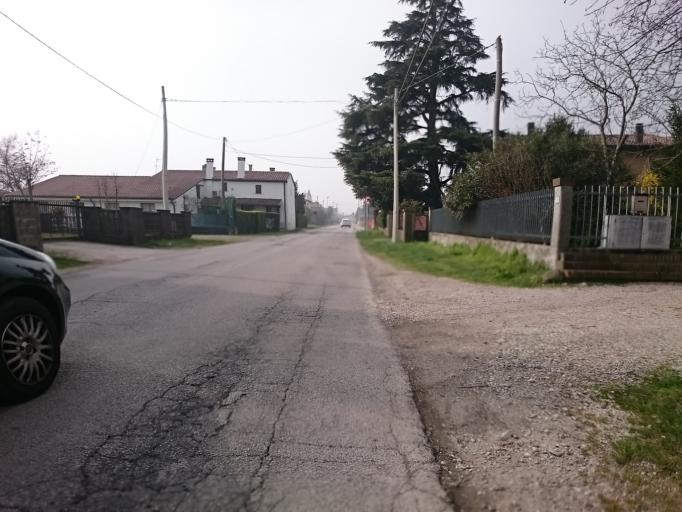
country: IT
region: Veneto
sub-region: Provincia di Padova
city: Bertipaglia
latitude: 45.3187
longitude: 11.8846
